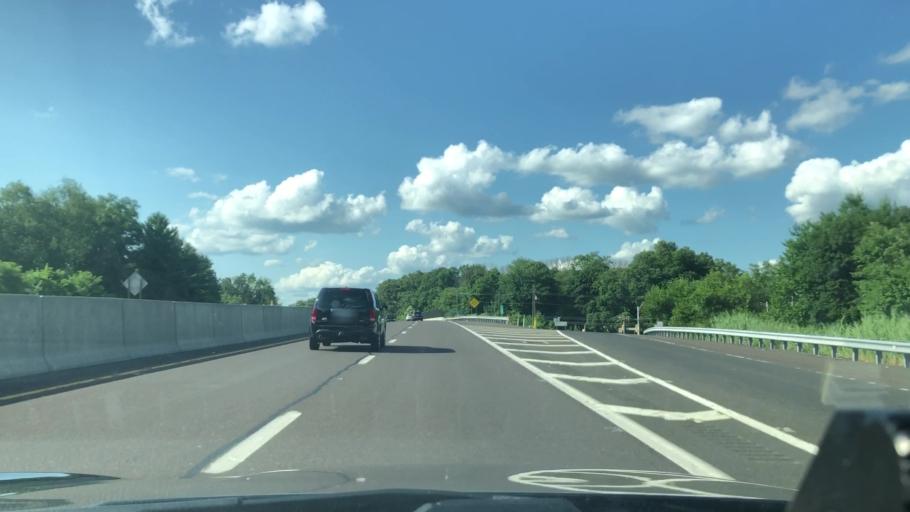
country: US
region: Pennsylvania
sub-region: Montgomery County
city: Fort Washington
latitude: 40.1599
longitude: -75.2012
